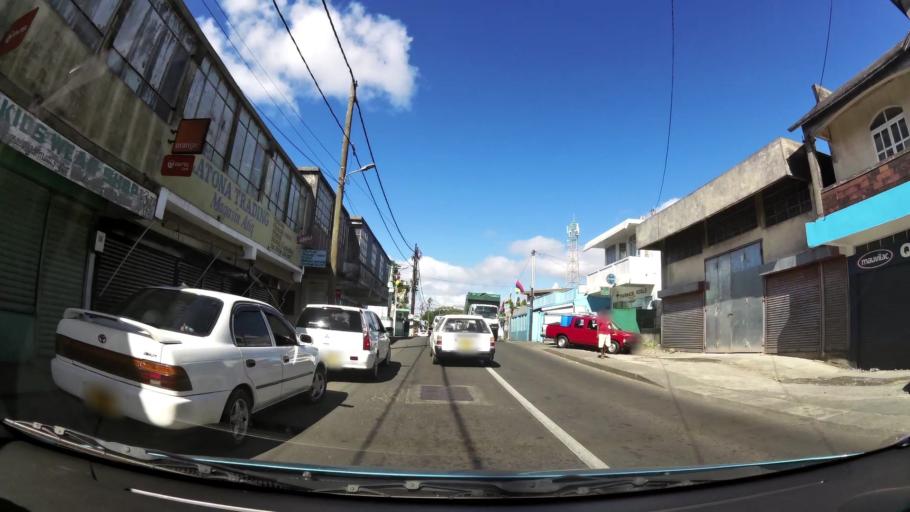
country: MU
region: Plaines Wilhems
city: Vacoas
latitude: -20.3220
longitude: 57.4848
